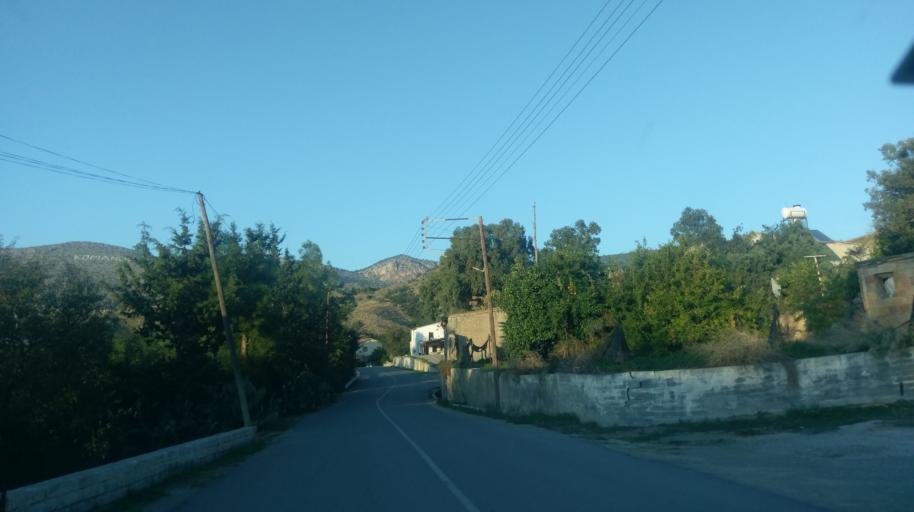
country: CY
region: Lefkosia
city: Nicosia
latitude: 35.2572
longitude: 33.4850
